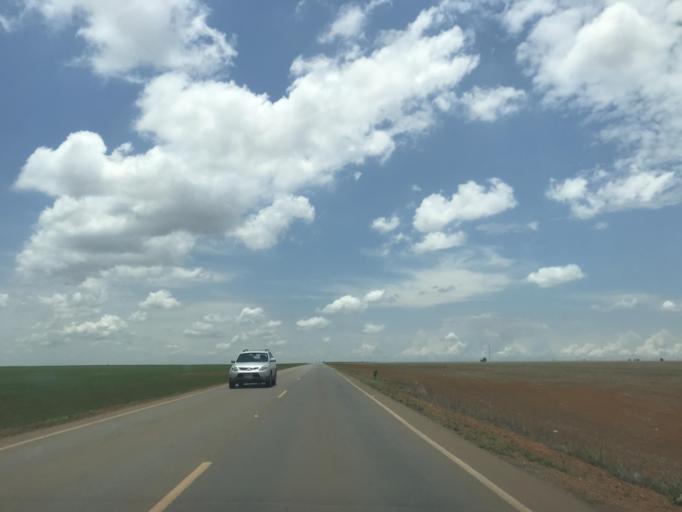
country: BR
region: Goias
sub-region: Vianopolis
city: Vianopolis
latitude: -16.5184
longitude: -48.2365
